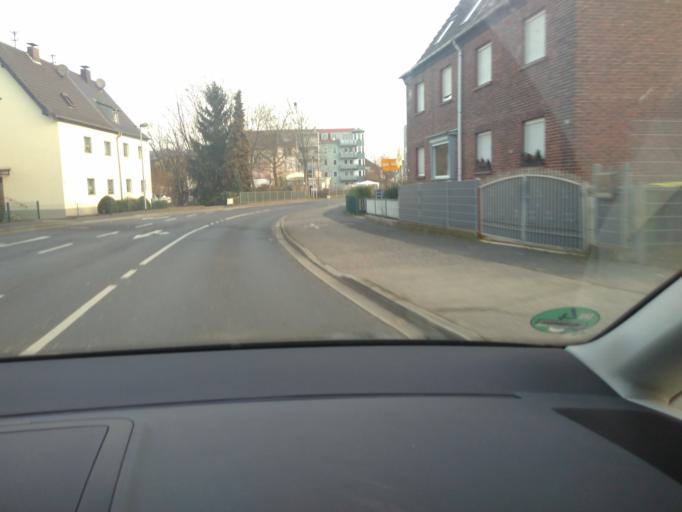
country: DE
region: North Rhine-Westphalia
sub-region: Regierungsbezirk Koln
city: Hennef
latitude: 50.7701
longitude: 7.2932
